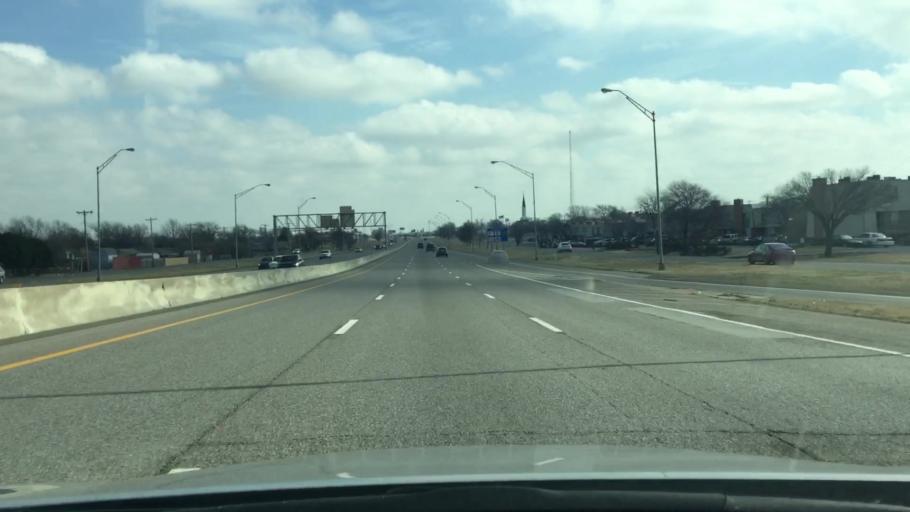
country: US
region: Oklahoma
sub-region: Oklahoma County
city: Oklahoma City
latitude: 35.3933
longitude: -97.5627
